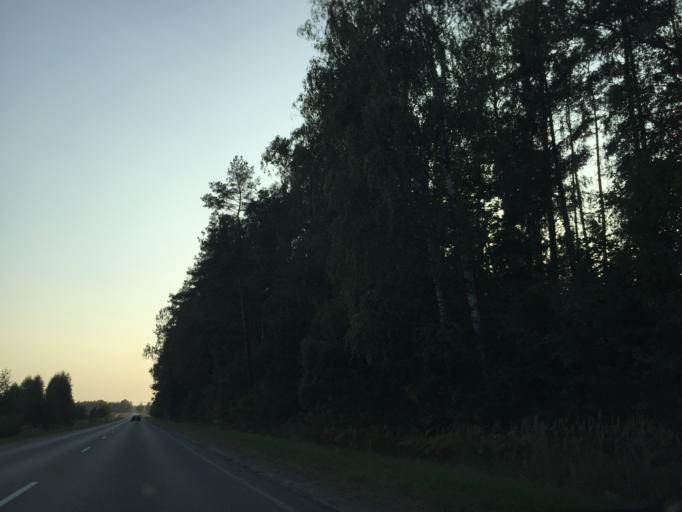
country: LV
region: Lielvarde
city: Lielvarde
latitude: 56.7808
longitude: 24.7891
